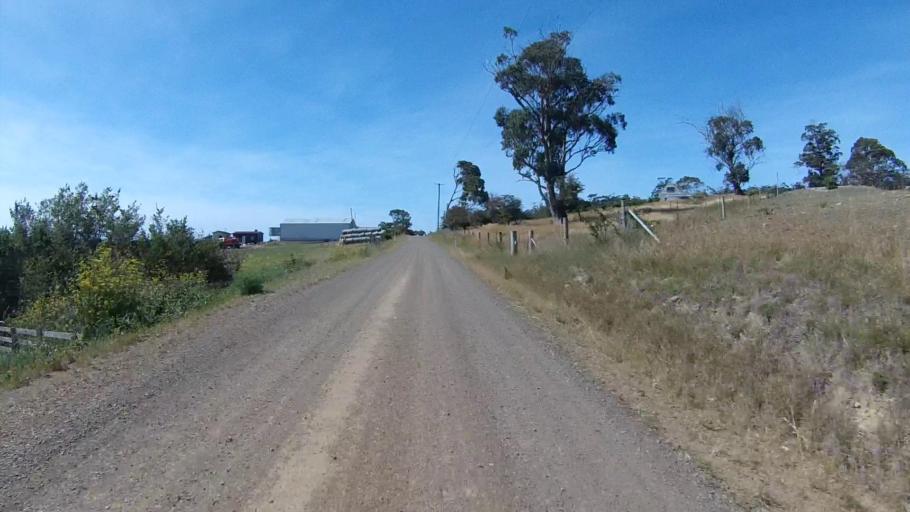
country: AU
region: Tasmania
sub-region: Sorell
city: Sorell
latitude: -42.7405
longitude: 147.5992
